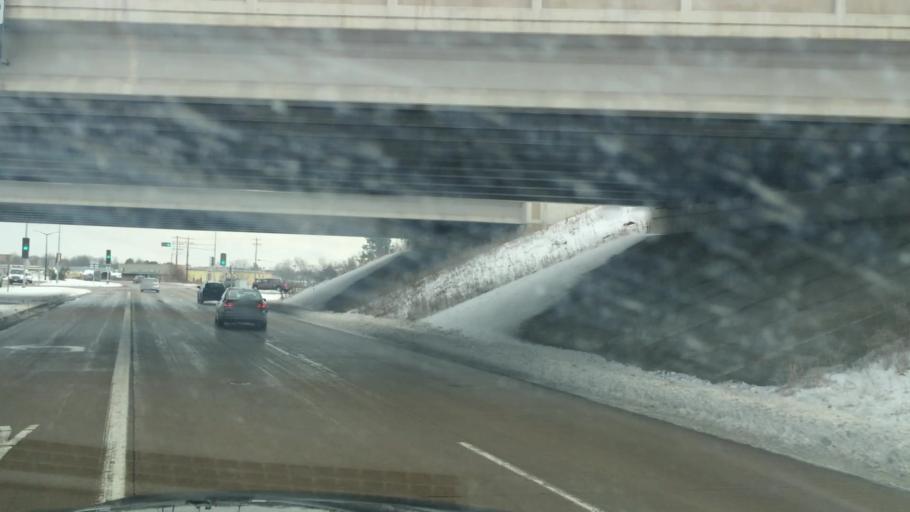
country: US
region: Wisconsin
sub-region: Marathon County
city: Rib Mountain
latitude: 44.9111
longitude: -89.6510
